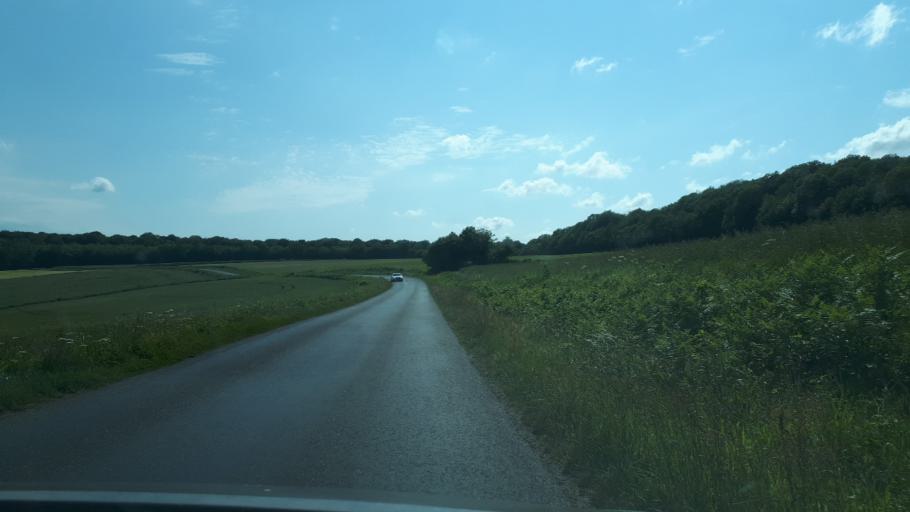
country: FR
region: Centre
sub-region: Departement du Cher
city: Henrichemont
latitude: 47.4021
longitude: 2.5981
